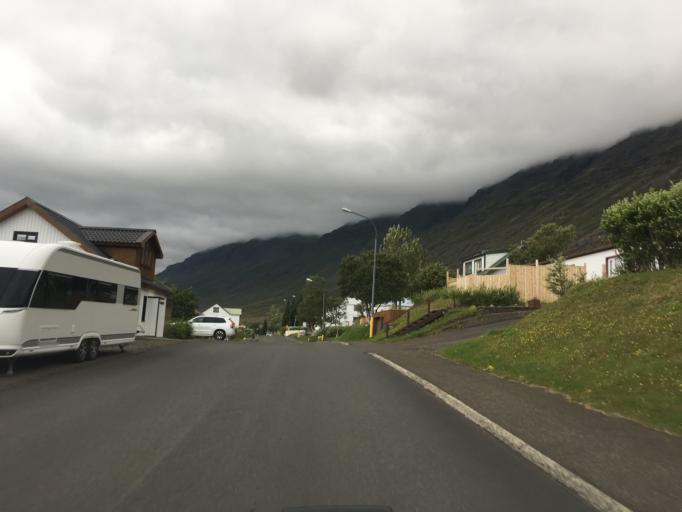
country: IS
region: East
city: Neskaupstadur
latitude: 65.1490
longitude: -13.6962
